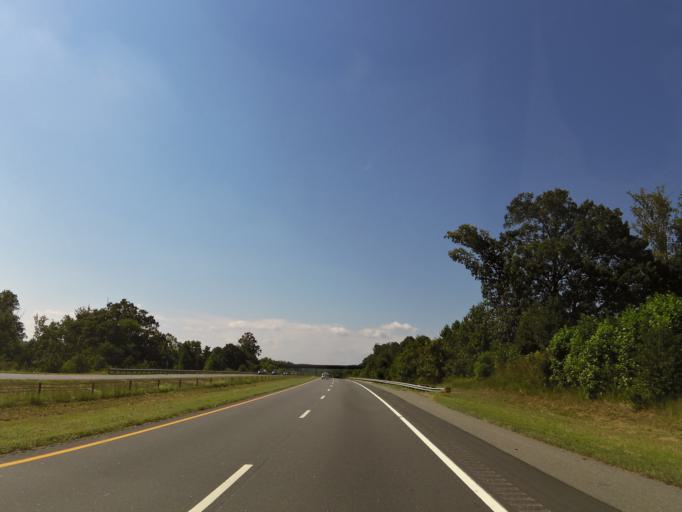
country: US
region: North Carolina
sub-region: Catawba County
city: Maiden
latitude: 35.6147
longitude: -81.2798
